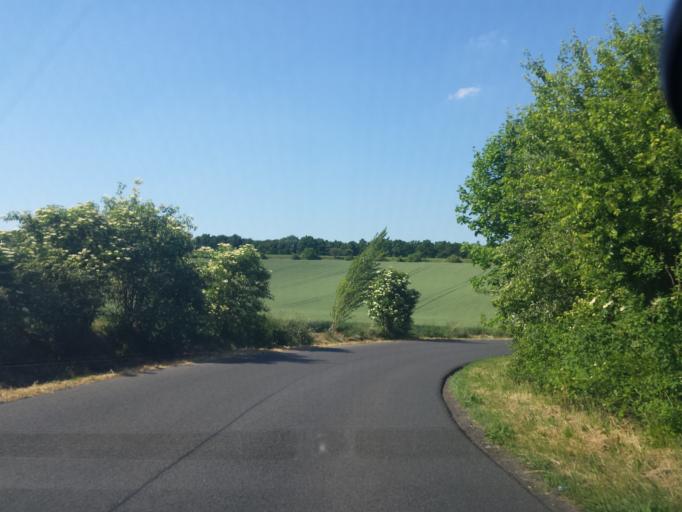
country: CZ
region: Central Bohemia
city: Nelahozeves
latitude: 50.2520
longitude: 14.2980
